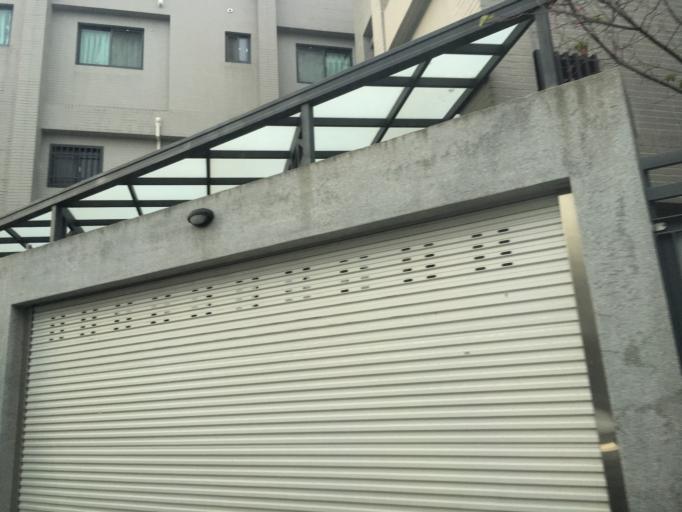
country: TW
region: Taiwan
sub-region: Taichung City
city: Taichung
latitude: 24.1723
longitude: 120.7331
